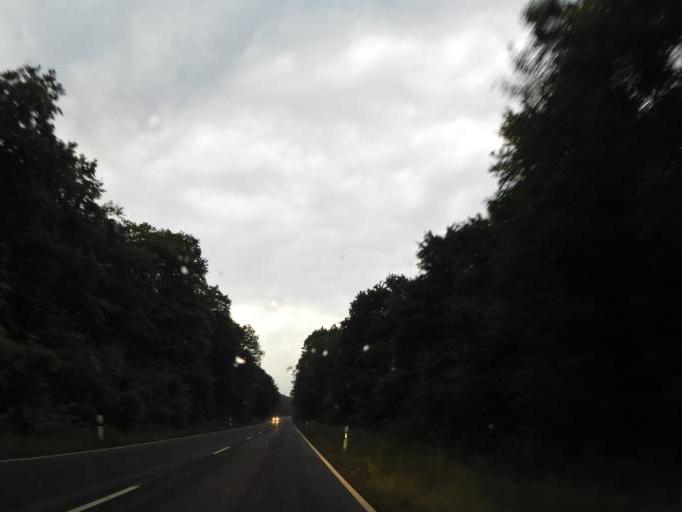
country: DE
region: Hesse
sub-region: Regierungsbezirk Darmstadt
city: Gross-Zimmern
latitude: 49.9052
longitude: 8.7906
